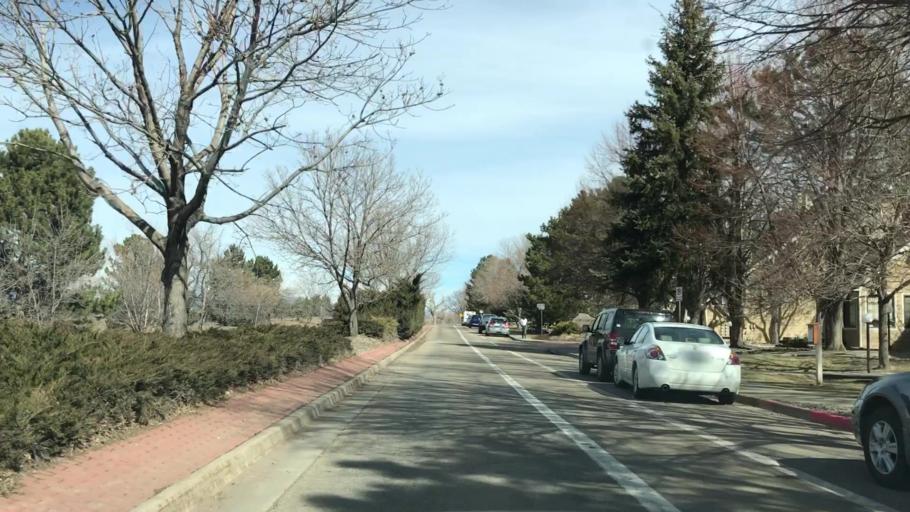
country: US
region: Colorado
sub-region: Boulder County
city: Gunbarrel
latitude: 40.0600
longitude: -105.2161
